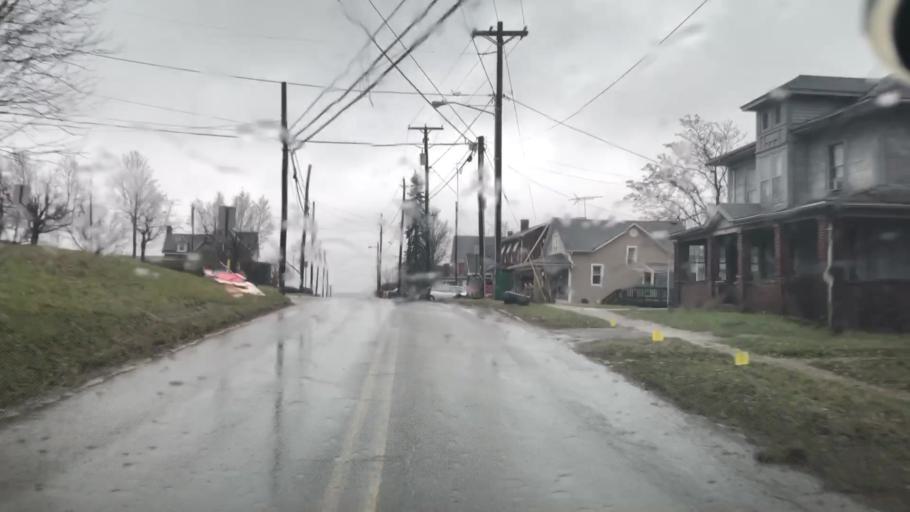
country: US
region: Ohio
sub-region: Harrison County
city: Cadiz
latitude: 40.2689
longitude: -80.9997
